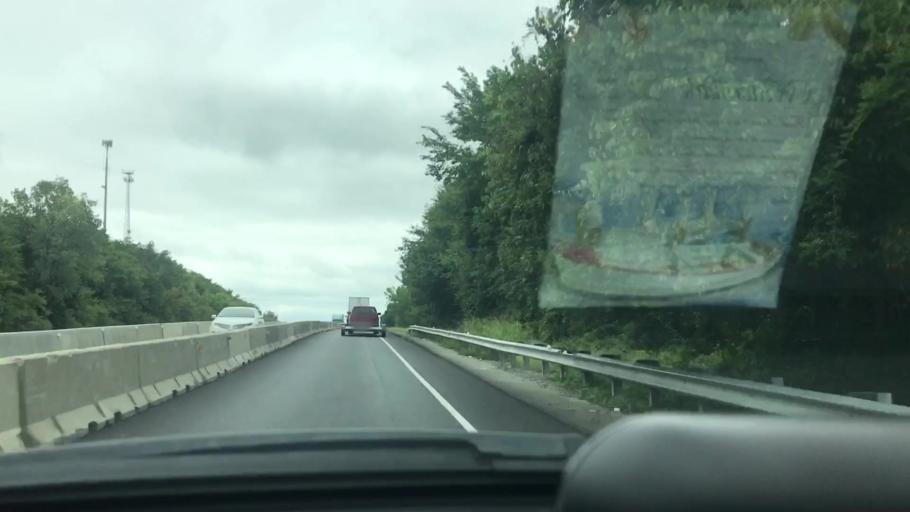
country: US
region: Oklahoma
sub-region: McIntosh County
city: Eufaula
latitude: 35.2864
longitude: -95.5930
